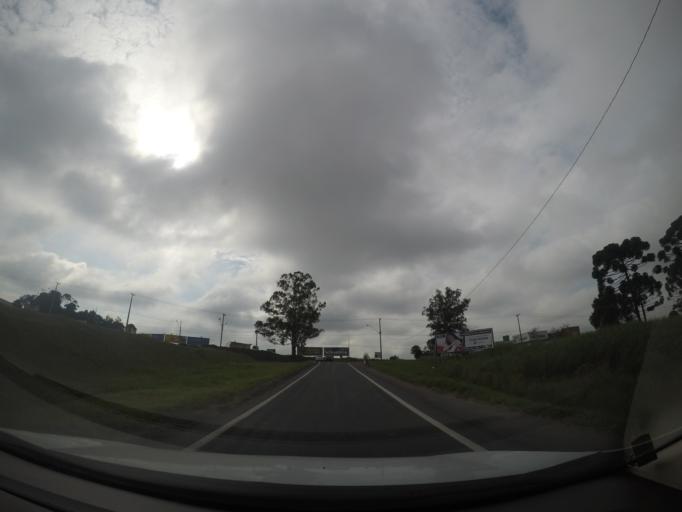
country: BR
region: Parana
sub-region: Colombo
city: Colombo
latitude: -25.3430
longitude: -49.2197
